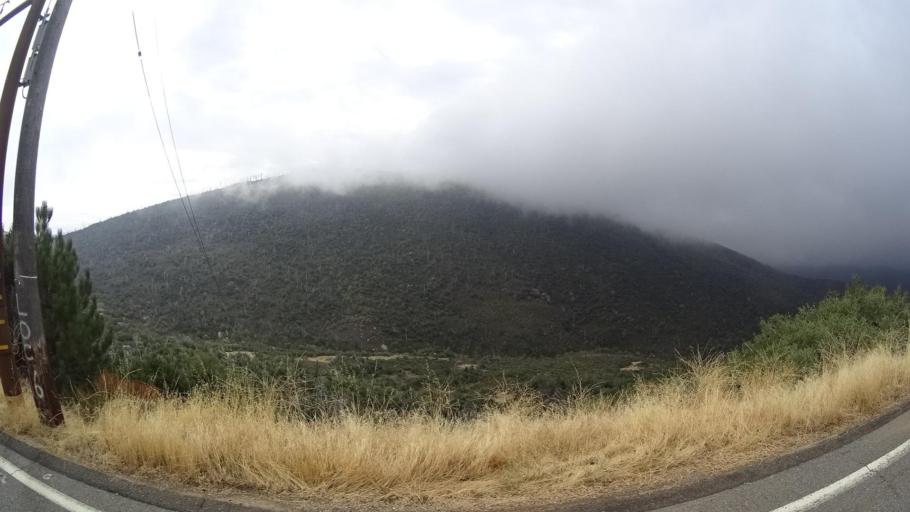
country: US
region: California
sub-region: San Diego County
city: Julian
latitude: 32.9975
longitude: -116.5952
